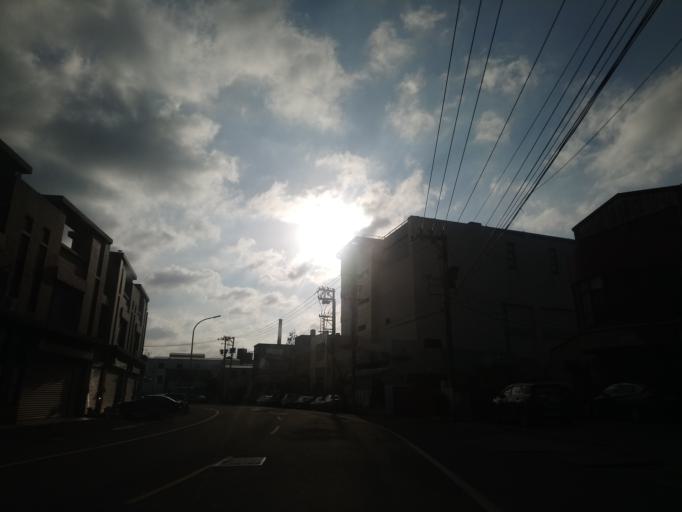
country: TW
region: Taiwan
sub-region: Hsinchu
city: Hsinchu
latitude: 24.7954
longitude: 120.9332
